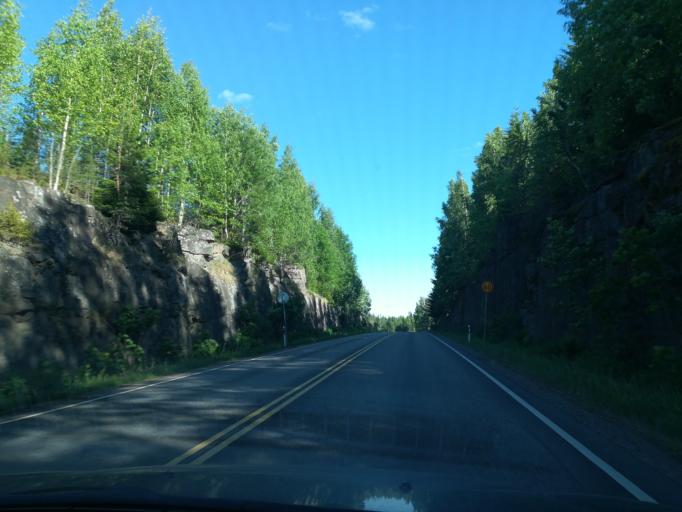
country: FI
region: South Karelia
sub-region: Imatra
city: Ruokolahti
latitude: 61.3554
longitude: 28.7197
